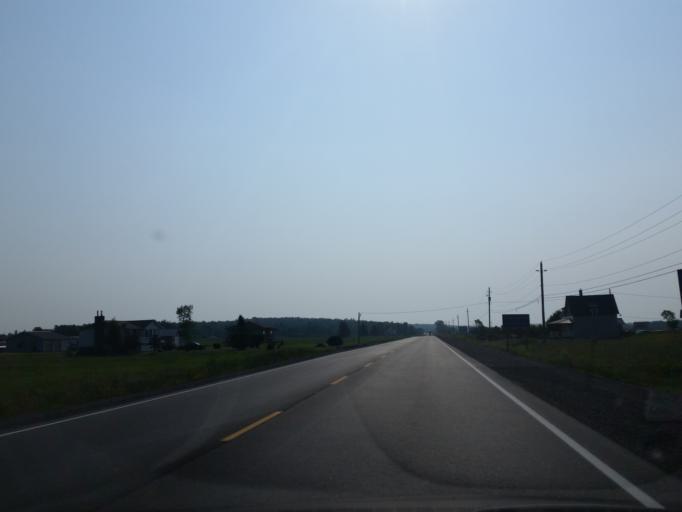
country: CA
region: Ontario
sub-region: Nipissing District
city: North Bay
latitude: 46.4070
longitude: -80.0711
